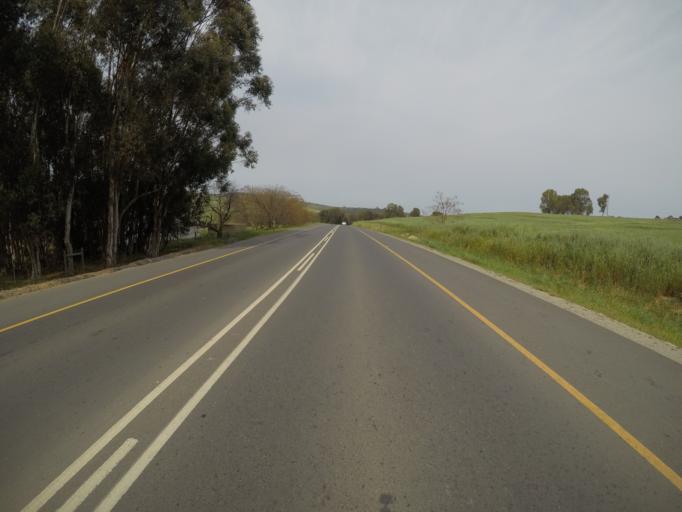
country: ZA
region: Western Cape
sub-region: West Coast District Municipality
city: Malmesbury
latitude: -33.4546
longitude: 18.7481
